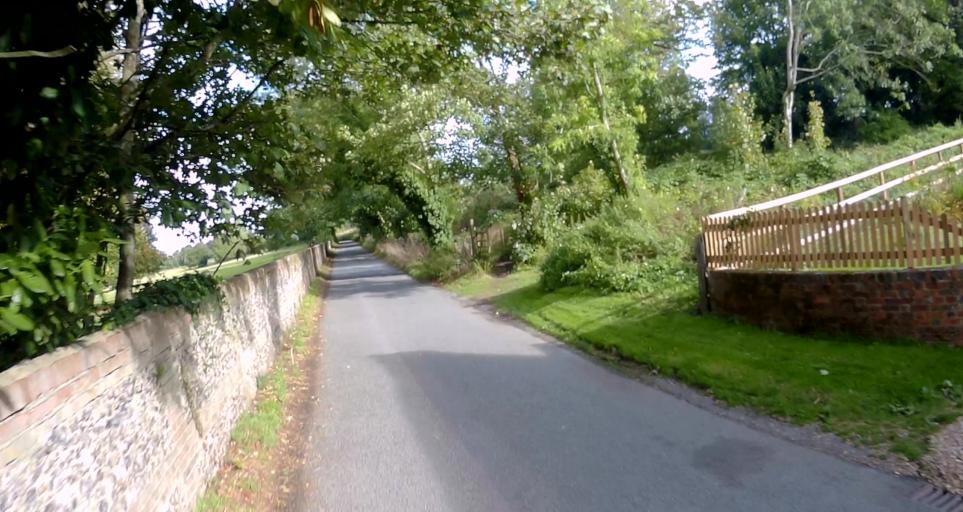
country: GB
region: England
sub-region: Hampshire
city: Kings Worthy
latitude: 51.0868
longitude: -1.2395
